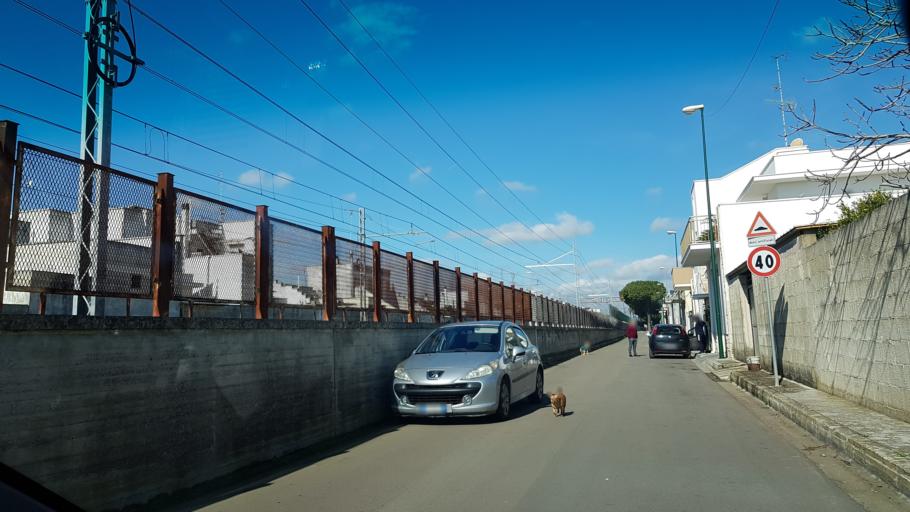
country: IT
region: Apulia
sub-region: Provincia di Lecce
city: Squinzano
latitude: 40.4325
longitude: 18.0533
